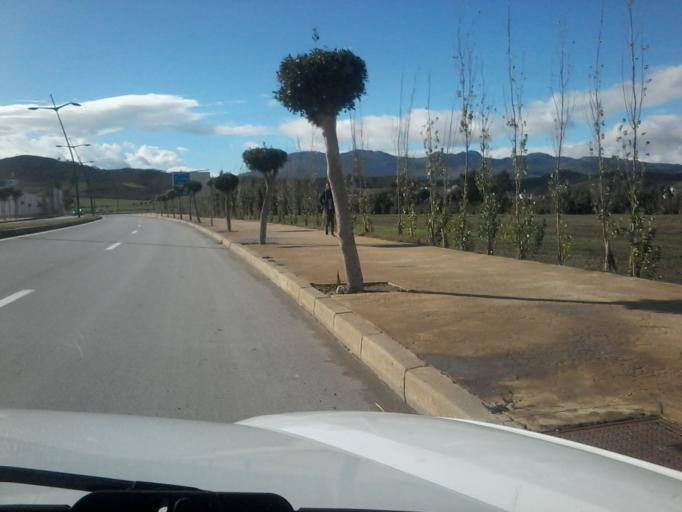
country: MA
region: Tanger-Tetouan
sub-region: Tetouan
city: Martil
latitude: 35.6944
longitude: -5.3385
